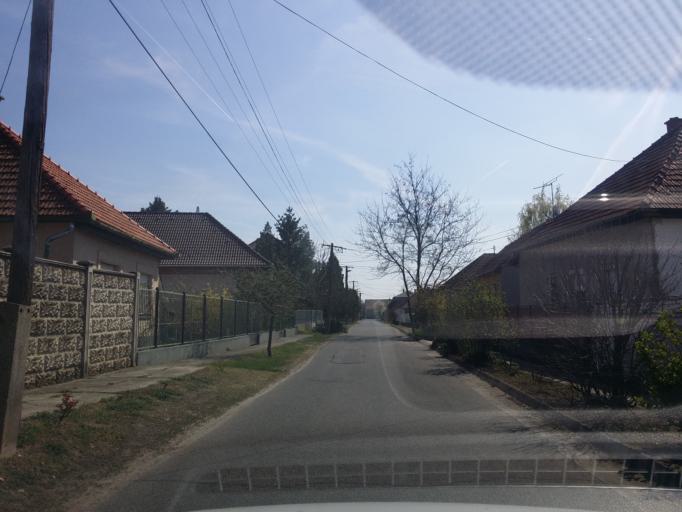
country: HU
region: Pest
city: Cegledbercel
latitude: 47.2148
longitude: 19.6811
